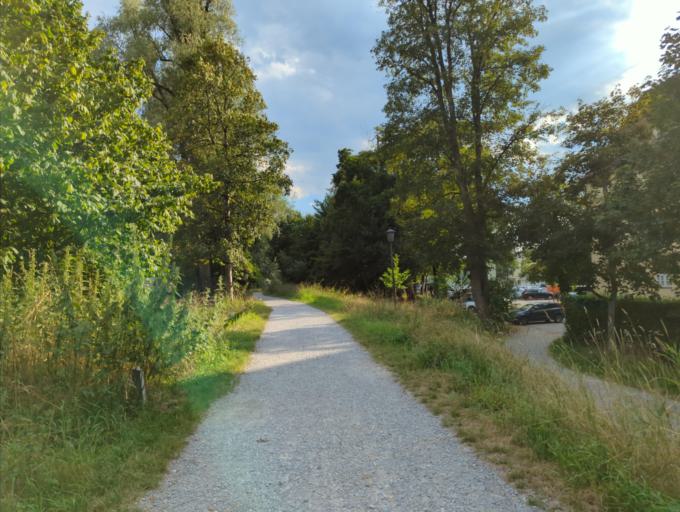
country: DE
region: Bavaria
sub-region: Upper Bavaria
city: Wasserburg am Inn
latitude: 48.0619
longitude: 12.2368
